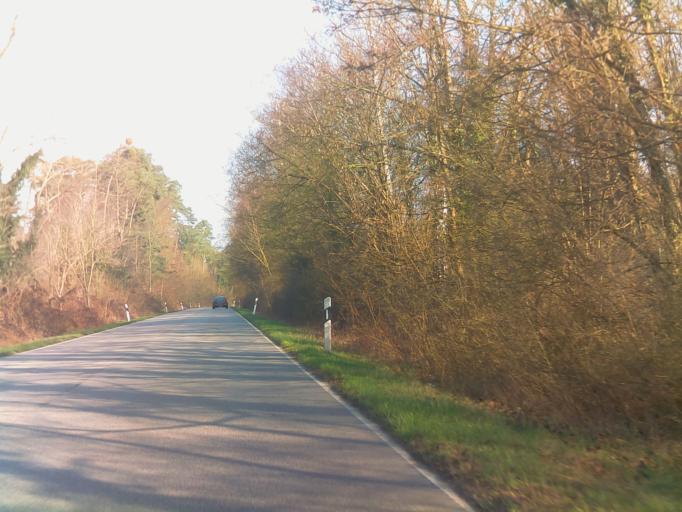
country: DE
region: Hesse
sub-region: Regierungsbezirk Darmstadt
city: Bickenbach
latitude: 49.7649
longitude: 8.6117
